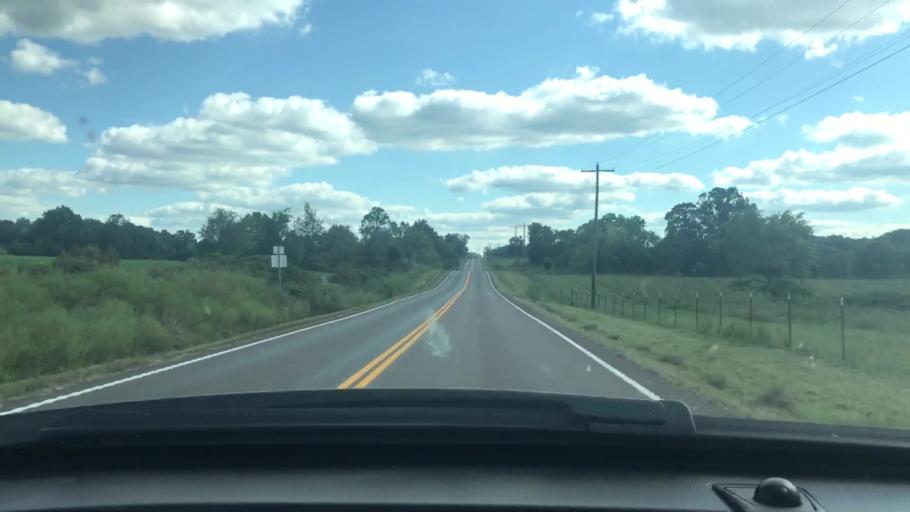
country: US
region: Missouri
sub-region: Wright County
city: Mountain Grove
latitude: 37.2411
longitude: -92.3005
